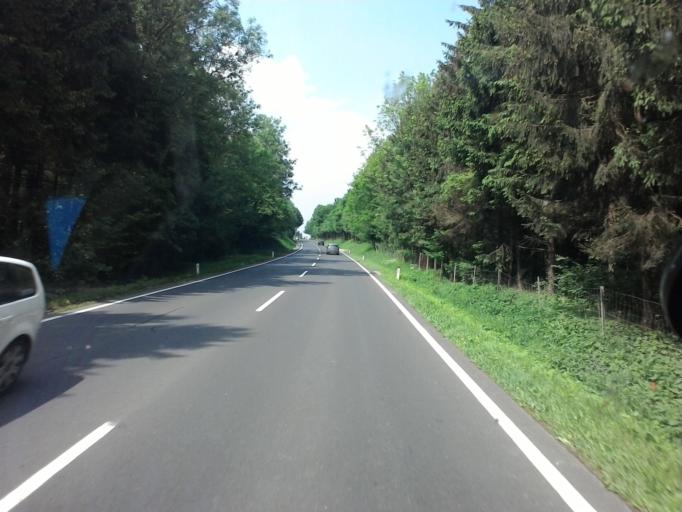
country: AT
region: Upper Austria
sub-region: Wels-Land
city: Steinhaus
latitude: 48.0972
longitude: 14.0411
